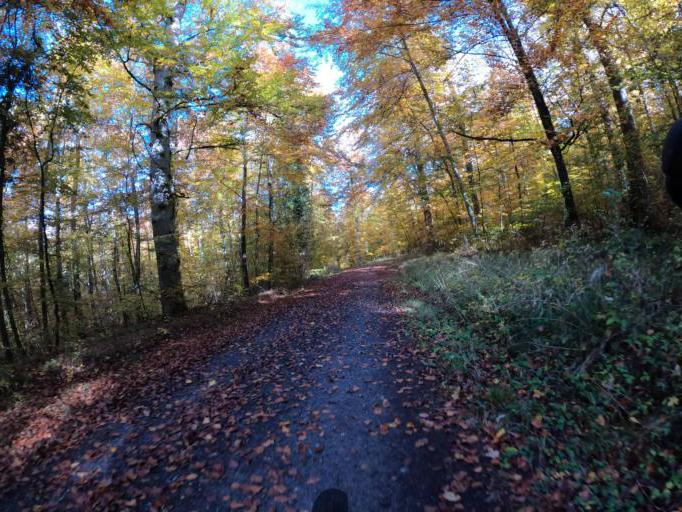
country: DE
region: Baden-Wuerttemberg
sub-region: Regierungsbezirk Stuttgart
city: Aidlingen
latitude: 48.6949
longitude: 8.9056
